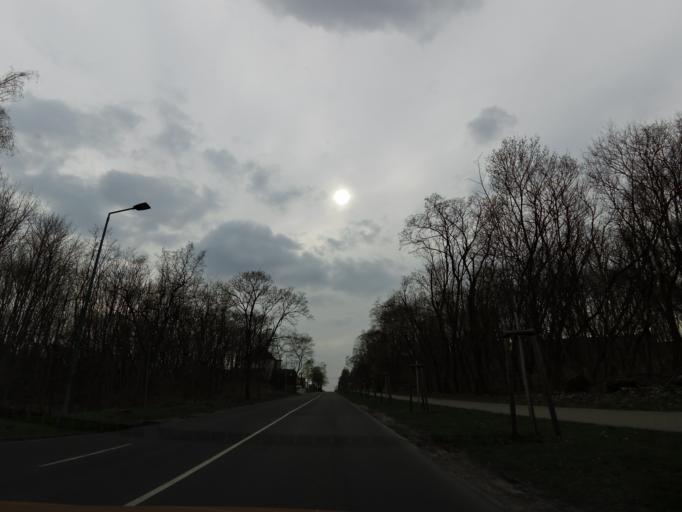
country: DE
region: Brandenburg
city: Frankfurt (Oder)
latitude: 52.3253
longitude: 14.5154
